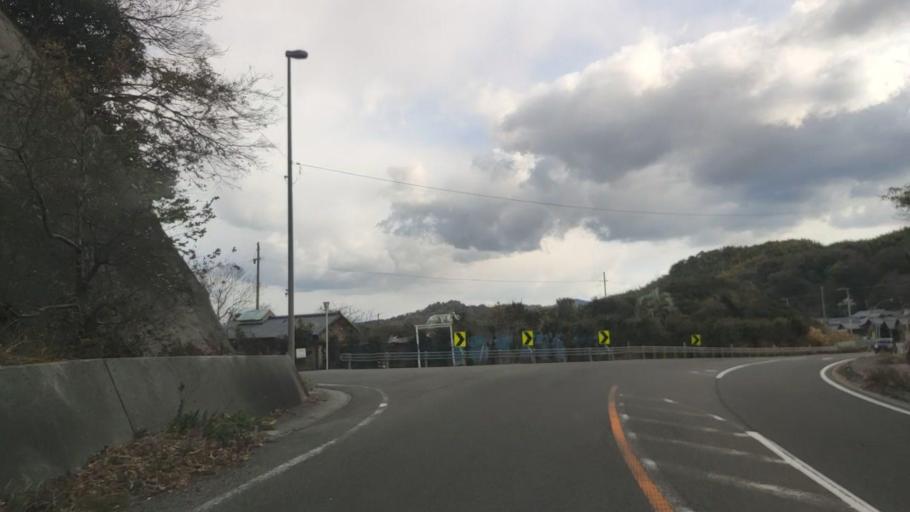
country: JP
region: Ehime
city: Hojo
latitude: 34.0327
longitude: 132.8305
